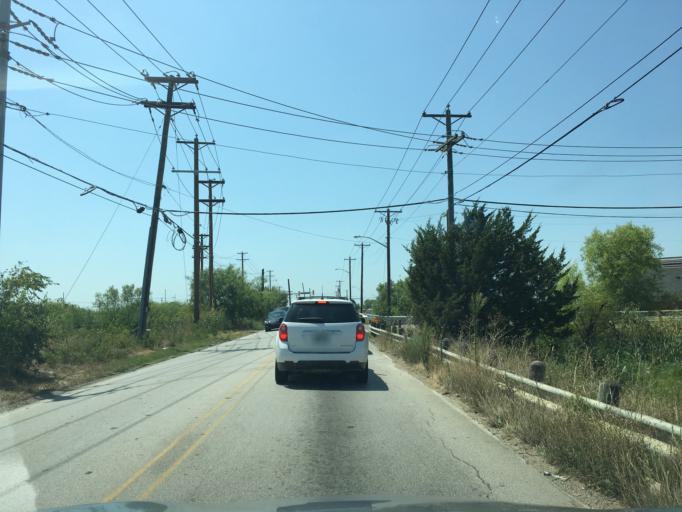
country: US
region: Texas
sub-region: Tarrant County
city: Crowley
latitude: 32.6142
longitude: -97.3481
